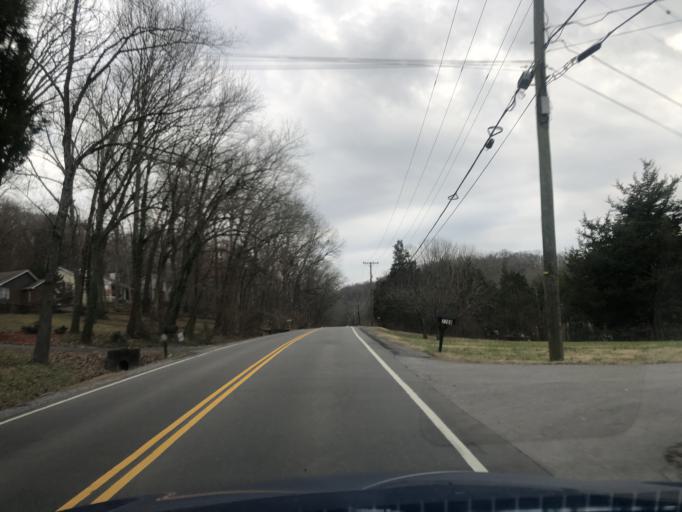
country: US
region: Tennessee
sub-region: Davidson County
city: Belle Meade
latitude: 36.0981
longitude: -86.9325
